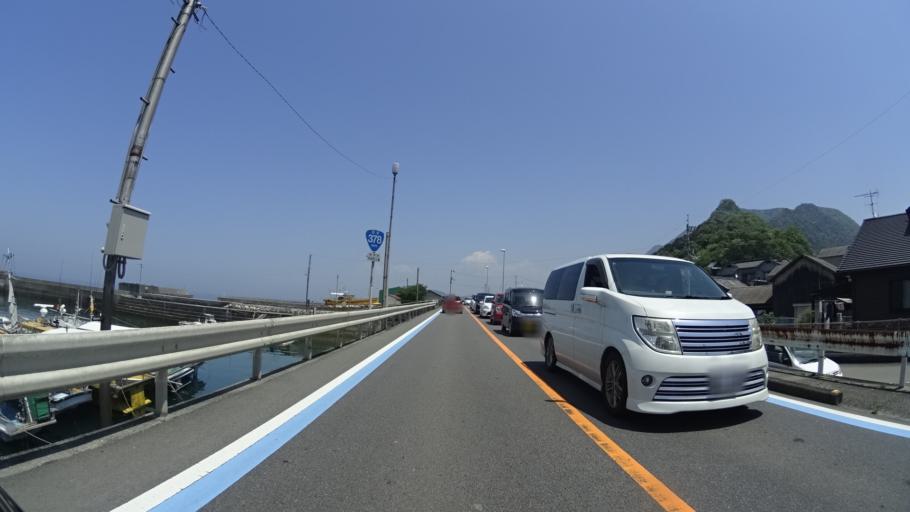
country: JP
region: Ehime
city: Iyo
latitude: 33.6887
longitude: 132.6378
